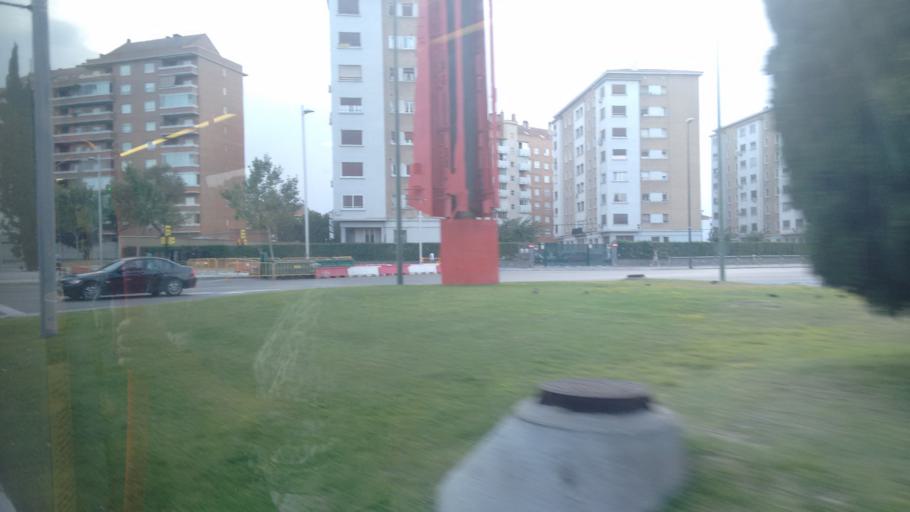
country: ES
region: Aragon
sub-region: Provincia de Zaragoza
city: Delicias
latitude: 41.6323
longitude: -0.9051
